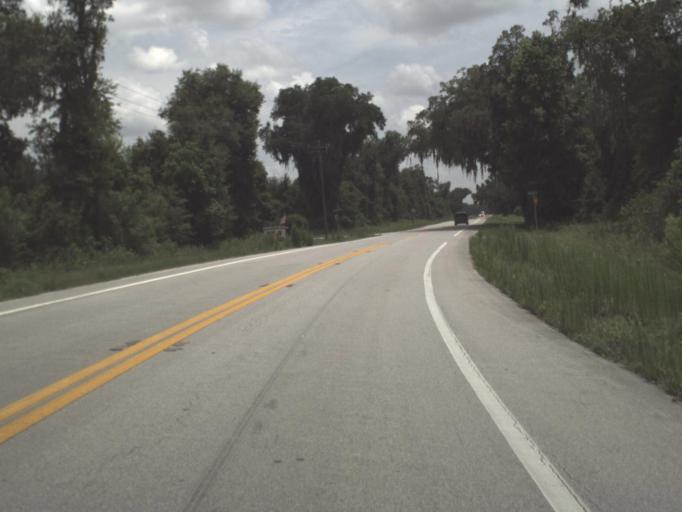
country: US
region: Florida
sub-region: Madison County
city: Madison
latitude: 30.5500
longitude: -83.4259
